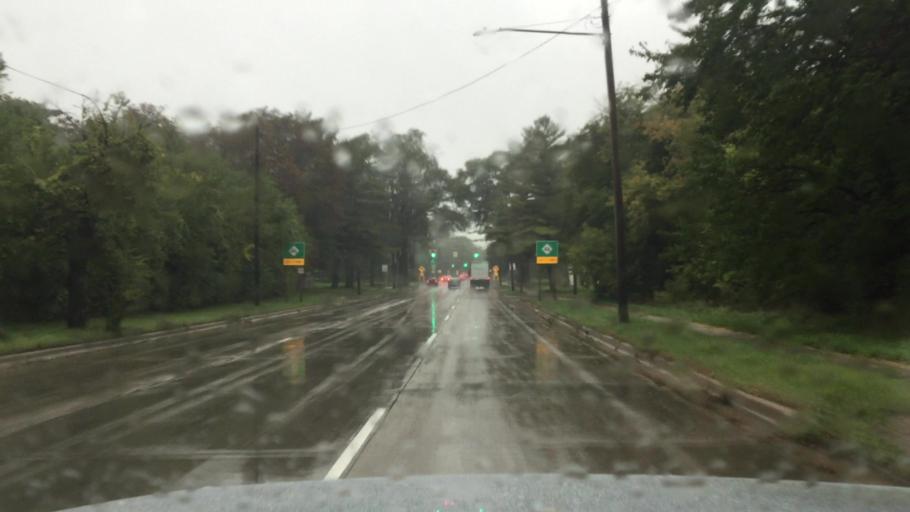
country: US
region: Michigan
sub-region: Saginaw County
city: Saginaw
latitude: 43.4161
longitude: -83.9317
